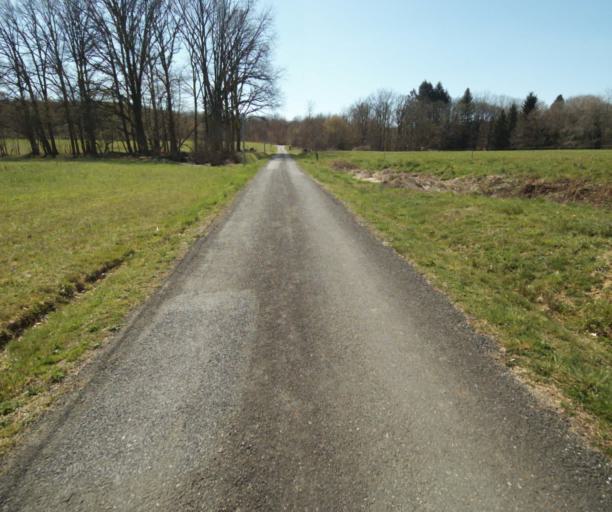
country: FR
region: Limousin
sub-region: Departement de la Correze
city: Chameyrat
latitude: 45.2711
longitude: 1.7096
